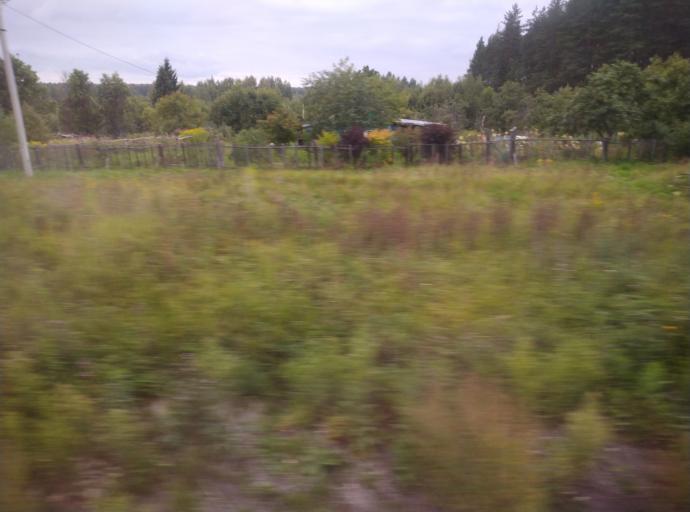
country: RU
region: Kostroma
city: Kosmynino
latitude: 57.5974
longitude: 40.7756
